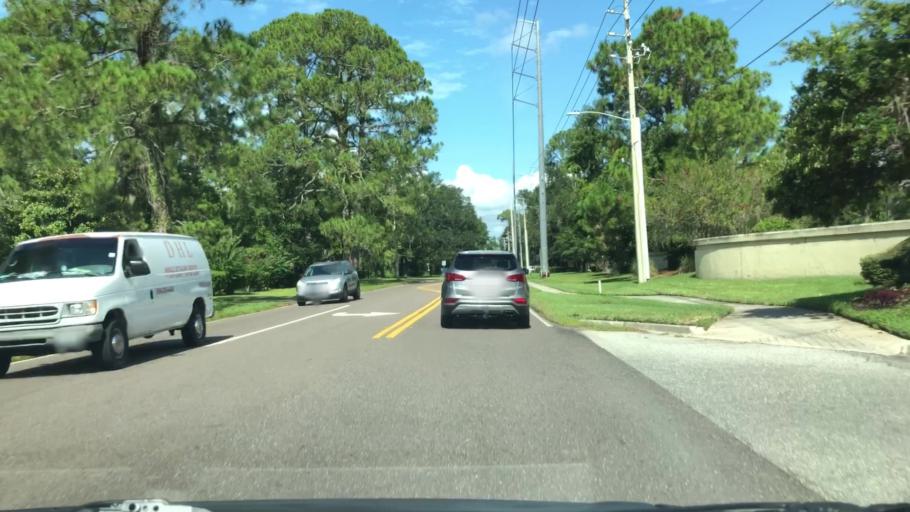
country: US
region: Florida
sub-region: Saint Johns County
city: Fruit Cove
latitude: 30.1839
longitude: -81.6096
